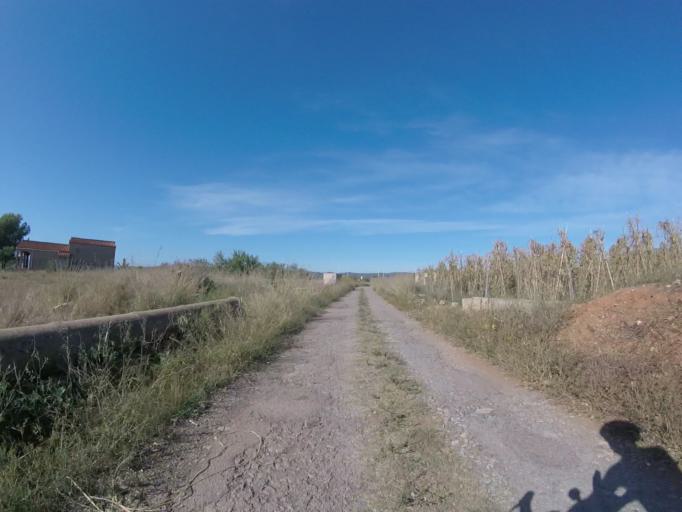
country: ES
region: Valencia
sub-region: Provincia de Castello
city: Torreblanca
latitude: 40.2102
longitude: 0.2266
